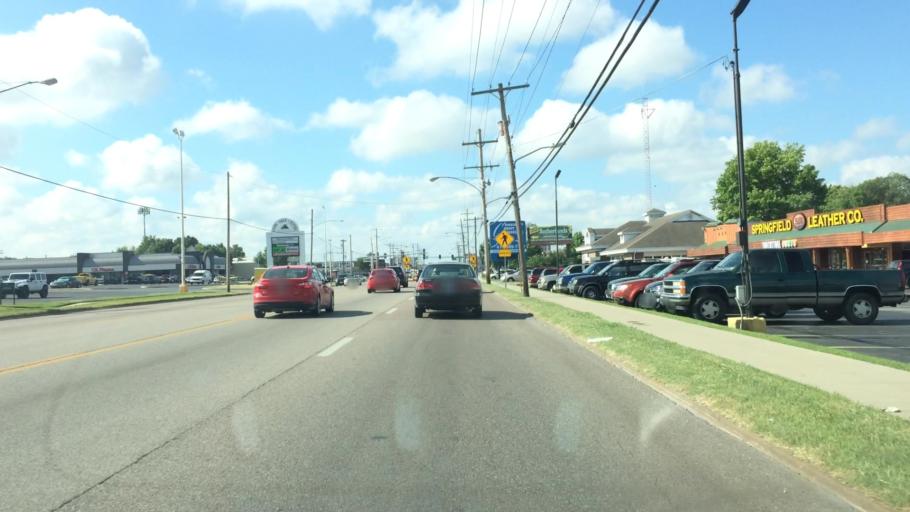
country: US
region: Missouri
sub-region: Greene County
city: Springfield
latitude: 37.1880
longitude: -93.2623
